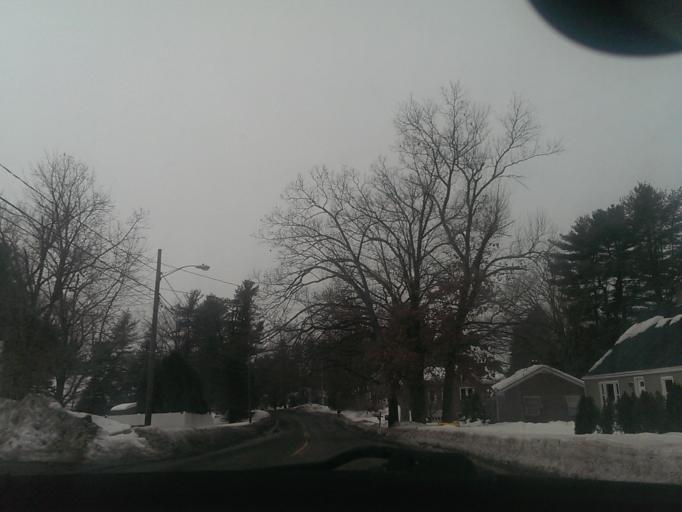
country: US
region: Massachusetts
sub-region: Hampden County
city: East Longmeadow
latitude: 42.0899
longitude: -72.4718
